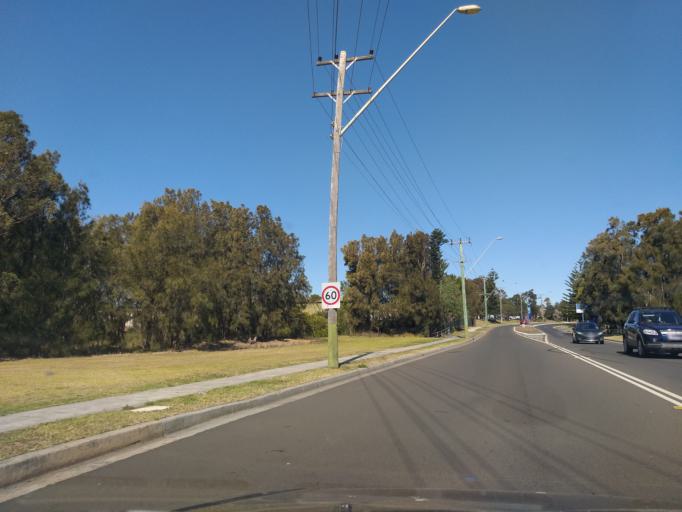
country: AU
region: New South Wales
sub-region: Wollongong
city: Corrimal
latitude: -34.3877
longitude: 150.9060
